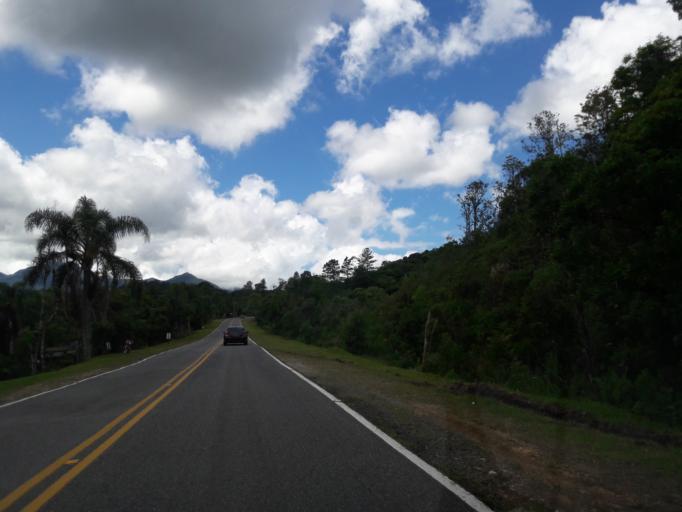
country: BR
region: Parana
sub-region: Campina Grande Do Sul
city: Campina Grande do Sul
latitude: -25.3096
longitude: -48.9399
